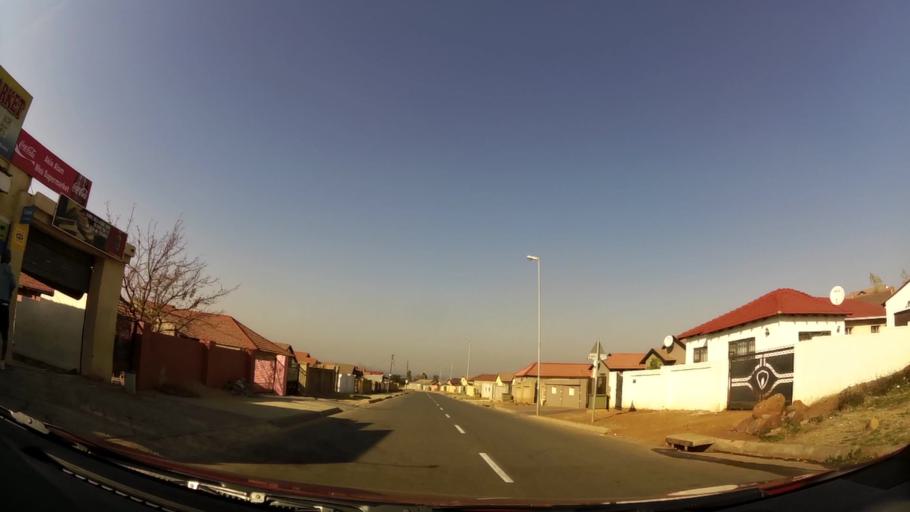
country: ZA
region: Gauteng
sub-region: City of Johannesburg Metropolitan Municipality
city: Soweto
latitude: -26.2989
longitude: 27.9498
